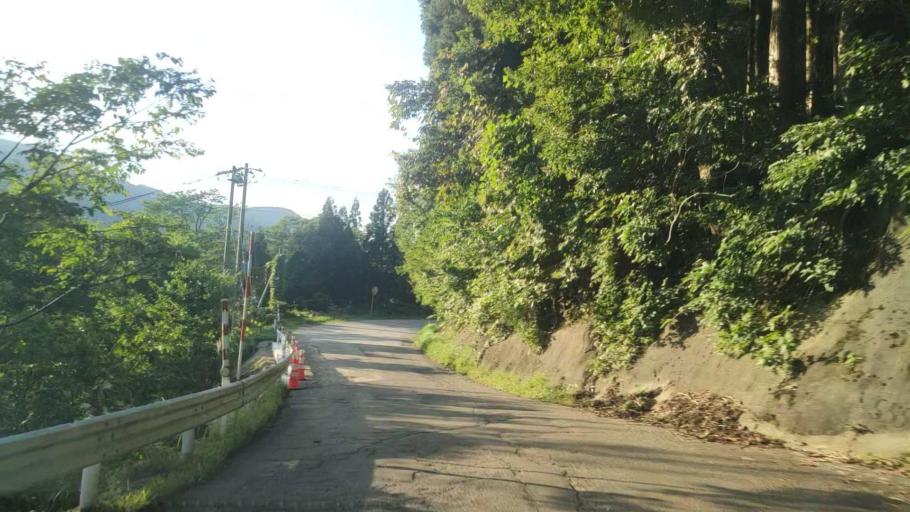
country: JP
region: Toyama
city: Yatsuomachi-higashikumisaka
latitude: 36.4820
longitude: 137.0309
